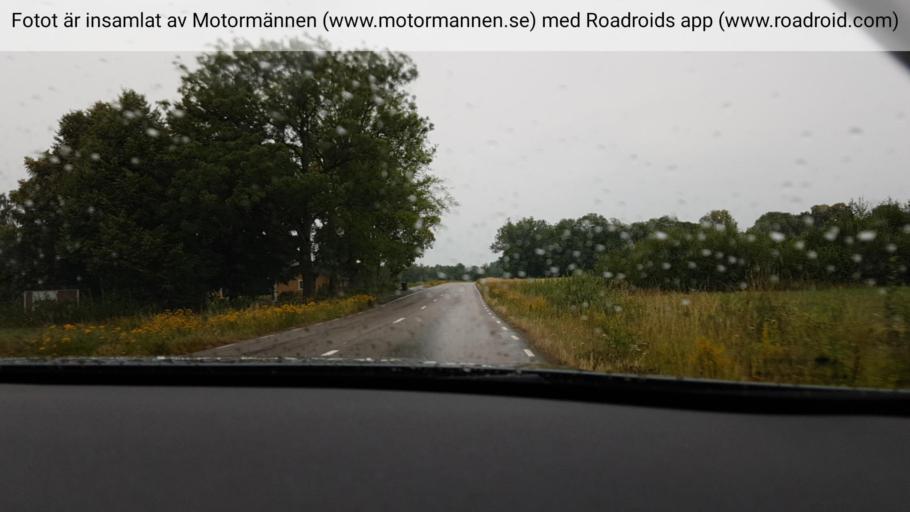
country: SE
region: Joenkoeping
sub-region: Varnamo Kommun
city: Varnamo
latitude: 57.1555
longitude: 14.0623
